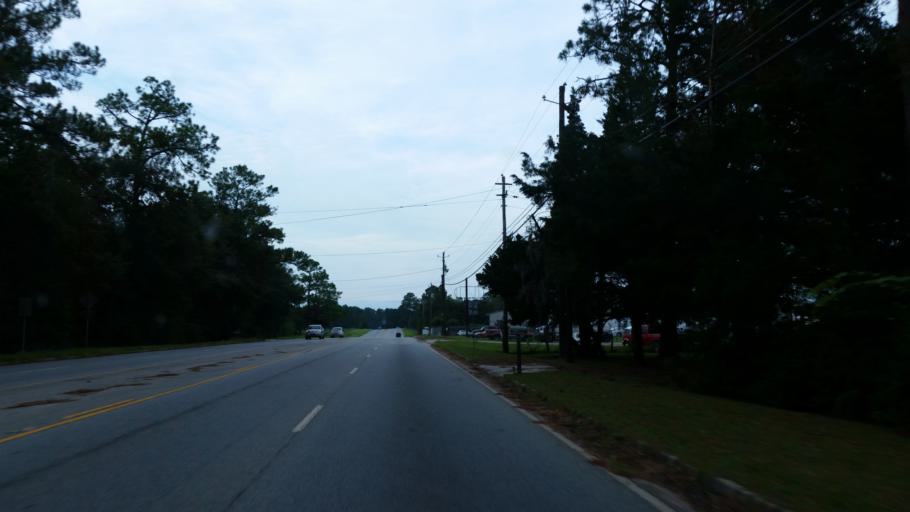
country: US
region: Georgia
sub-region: Lowndes County
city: Valdosta
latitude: 30.7566
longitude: -83.2709
